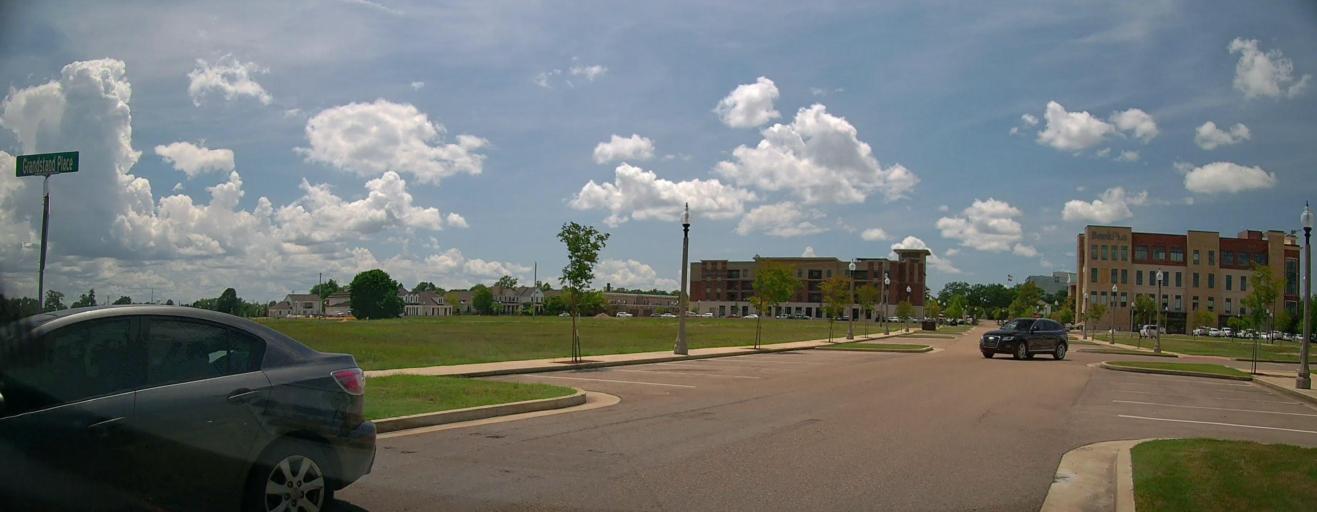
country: US
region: Mississippi
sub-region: Lee County
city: Tupelo
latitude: 34.2564
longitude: -88.6990
